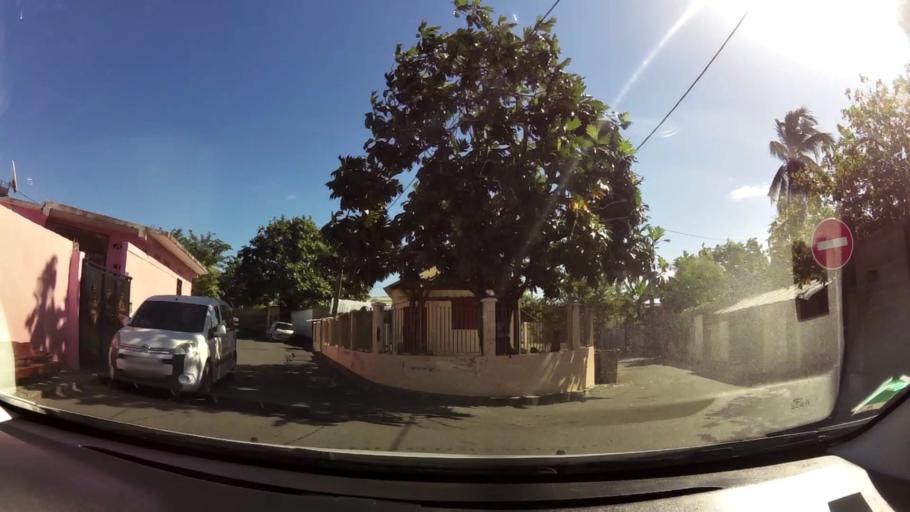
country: YT
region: Dzaoudzi
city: Dzaoudzi
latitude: -12.7868
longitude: 45.2696
